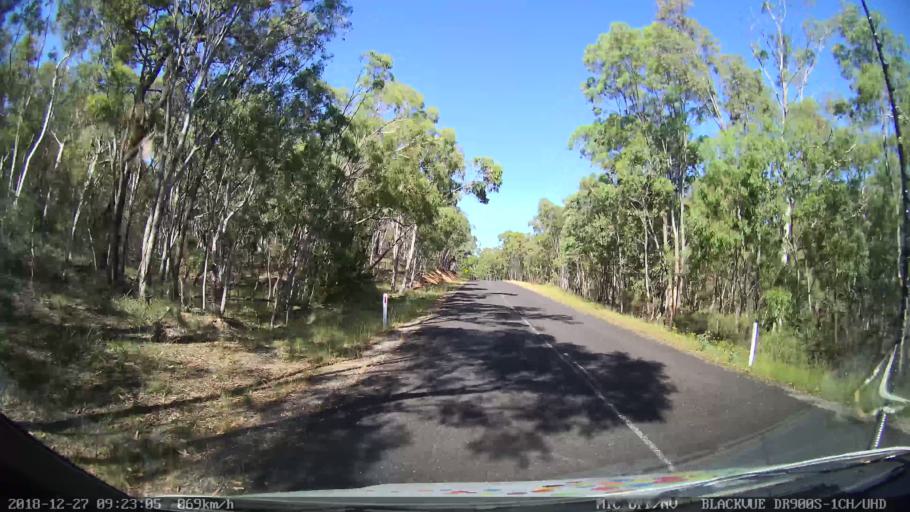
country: AU
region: New South Wales
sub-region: Lithgow
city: Portland
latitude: -33.1240
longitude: 150.0010
